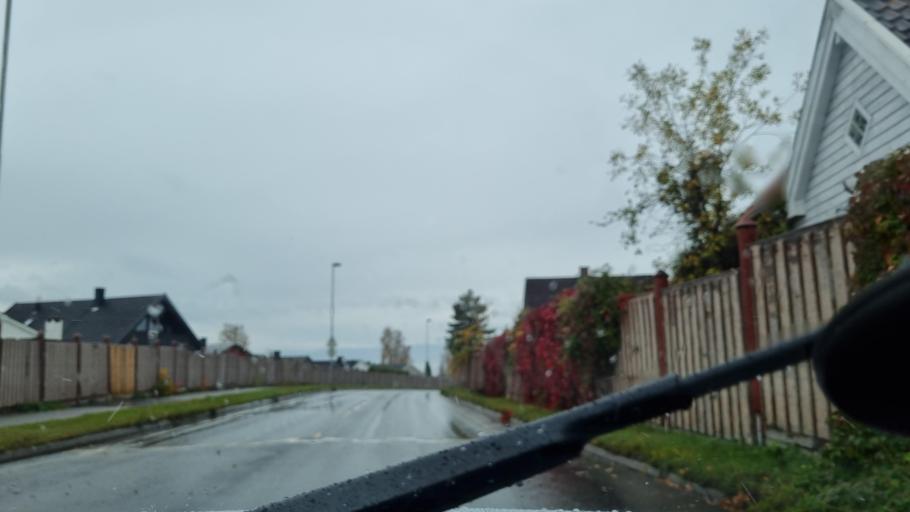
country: NO
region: Hedmark
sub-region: Hamar
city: Hamar
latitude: 60.8125
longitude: 11.0607
